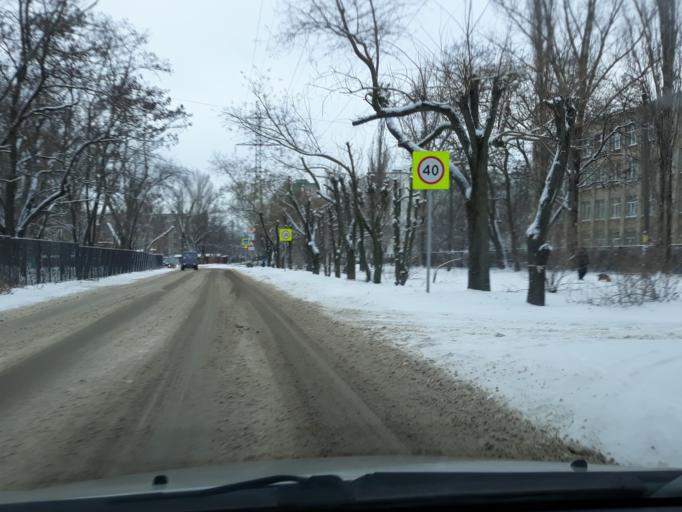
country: RU
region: Rostov
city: Taganrog
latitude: 47.2379
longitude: 38.8747
